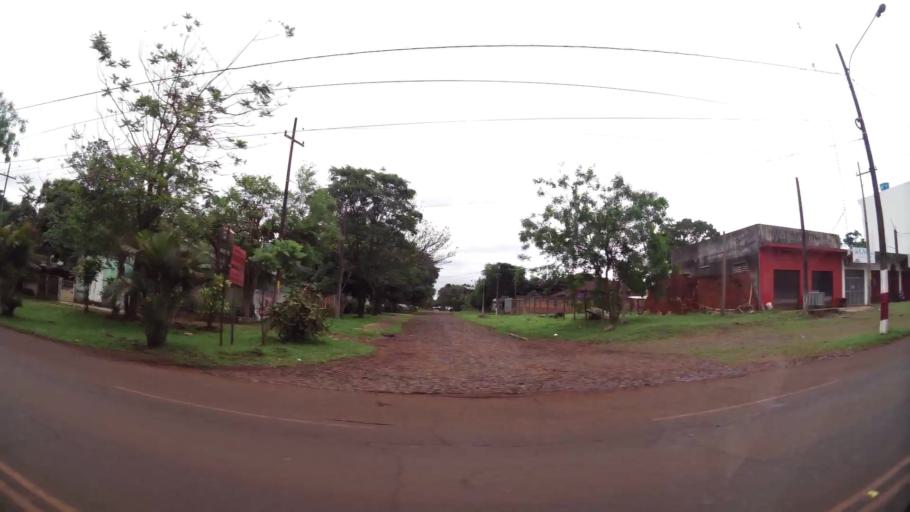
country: PY
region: Alto Parana
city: Ciudad del Este
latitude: -25.4102
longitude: -54.6329
